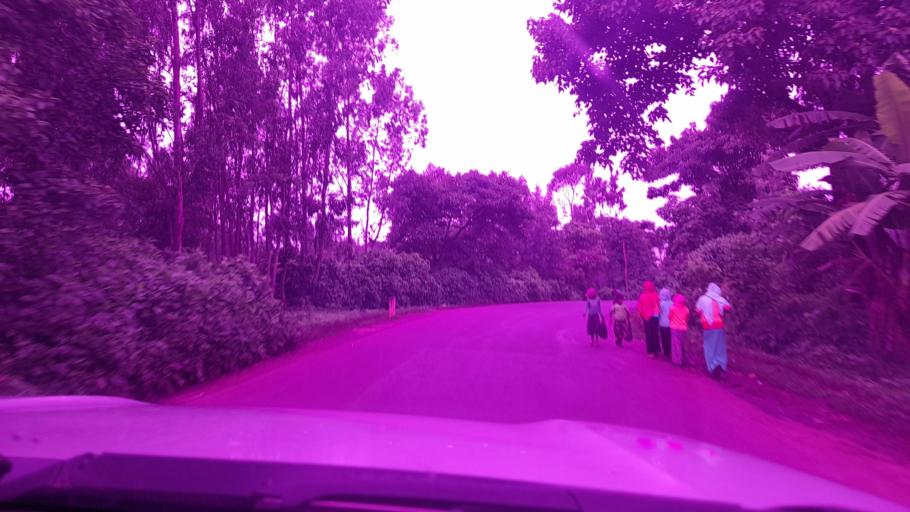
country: ET
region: Oromiya
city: Jima
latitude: 7.9237
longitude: 37.4127
